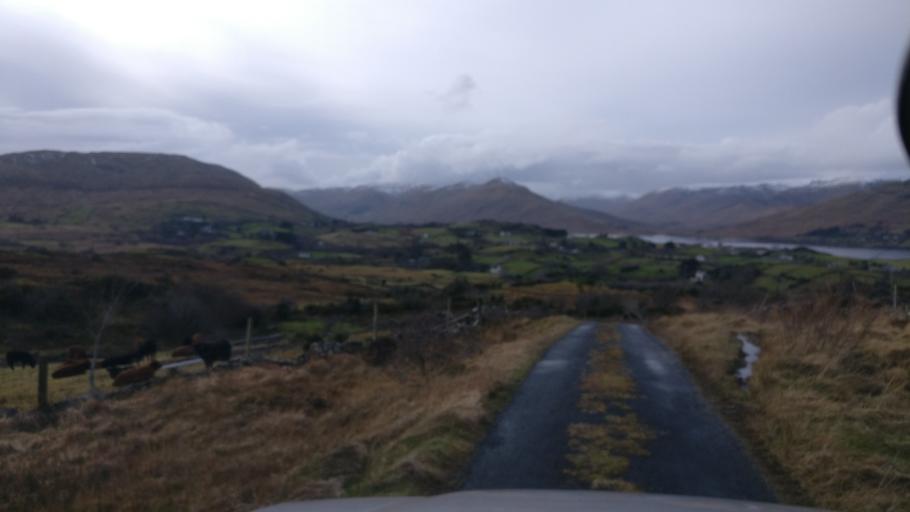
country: IE
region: Connaught
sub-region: County Galway
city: Oughterard
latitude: 53.5511
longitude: -9.4370
